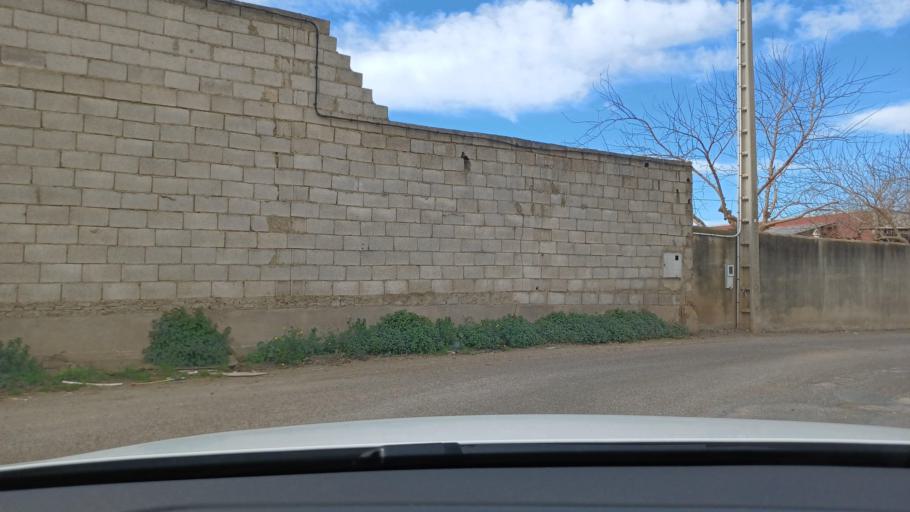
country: ES
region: Valencia
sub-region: Provincia de Valencia
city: Benifaio
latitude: 39.2884
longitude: -0.4333
